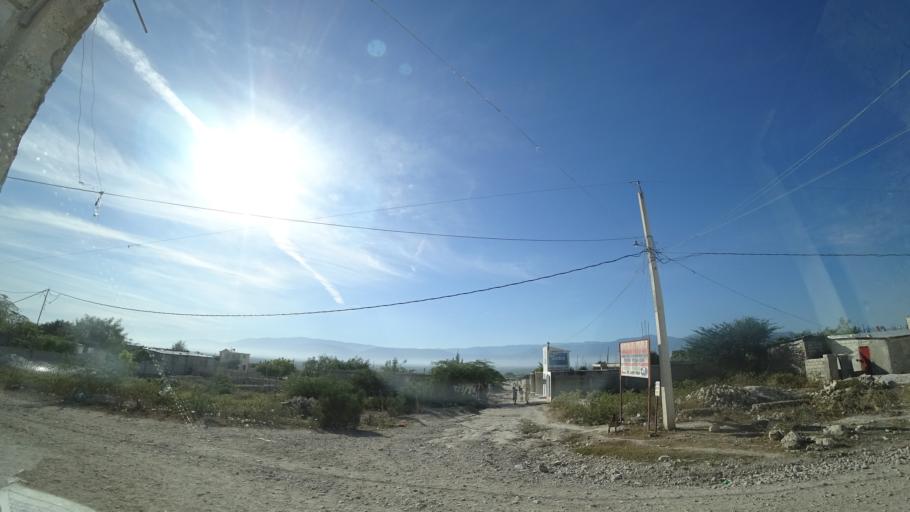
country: HT
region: Ouest
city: Croix des Bouquets
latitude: 18.6665
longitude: -72.2333
